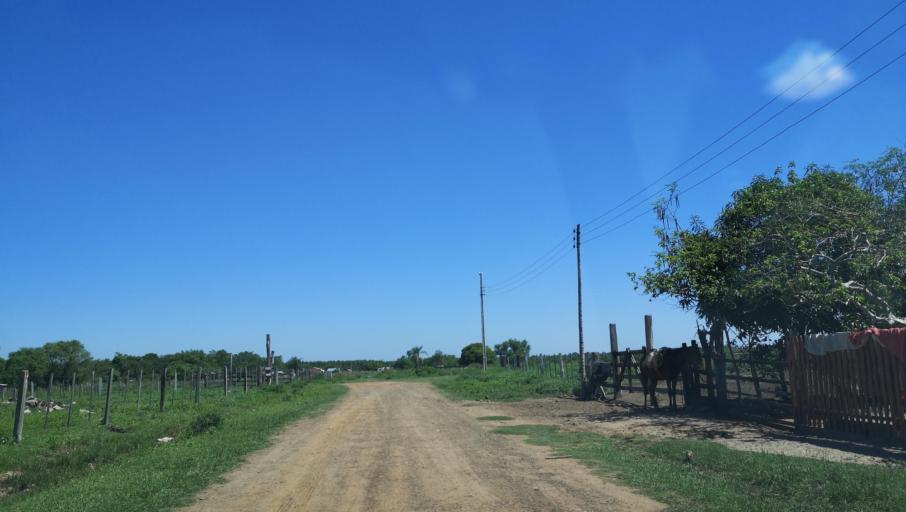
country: PY
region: Caaguazu
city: Carayao
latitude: -25.1919
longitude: -56.4043
